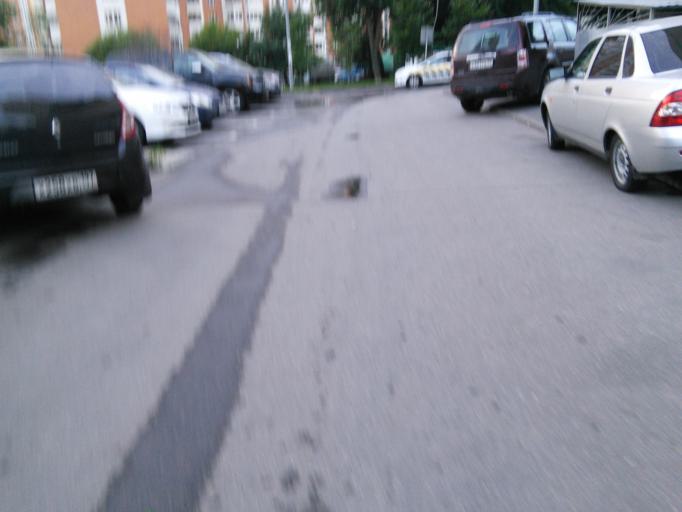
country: RU
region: Moscow
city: Leonovo
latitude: 55.8540
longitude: 37.6487
